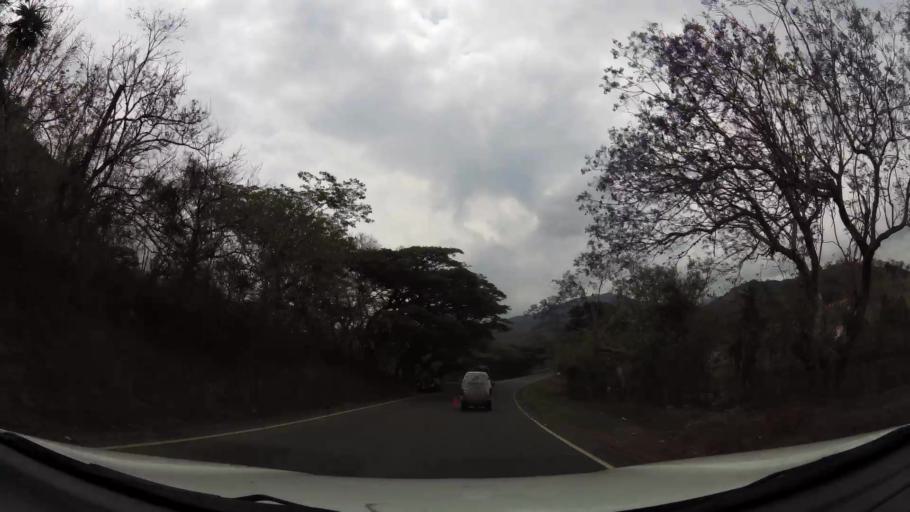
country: NI
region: Matagalpa
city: Matagalpa
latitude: 12.9541
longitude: -85.9200
